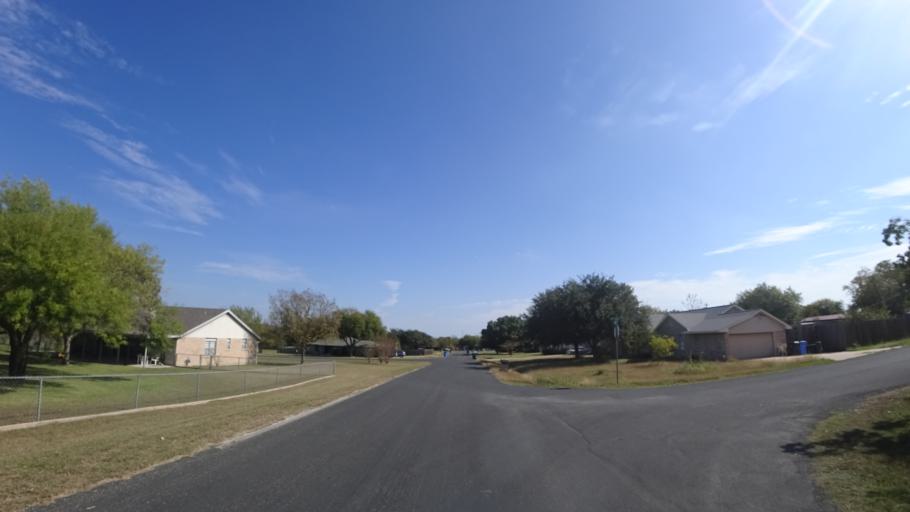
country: US
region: Texas
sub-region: Travis County
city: Pflugerville
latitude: 30.4122
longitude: -97.6284
